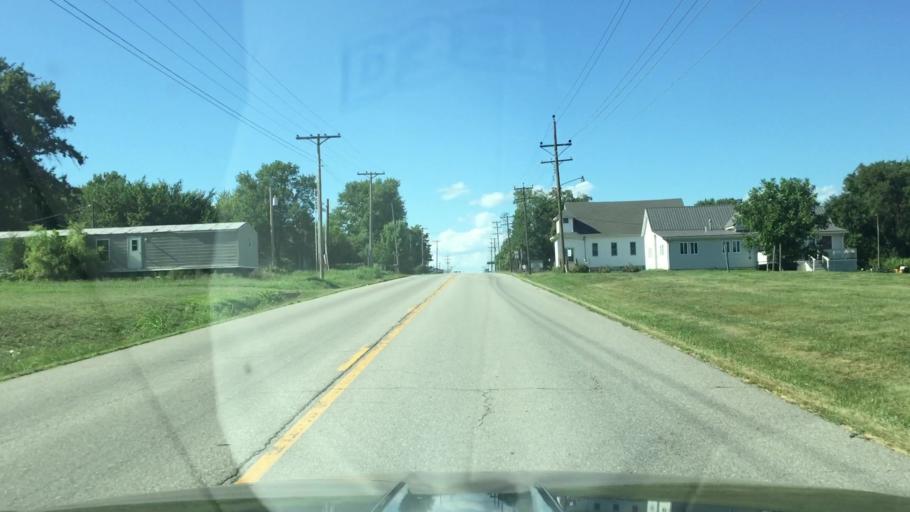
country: US
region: Missouri
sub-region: Moniteau County
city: Tipton
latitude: 38.5658
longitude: -92.7970
